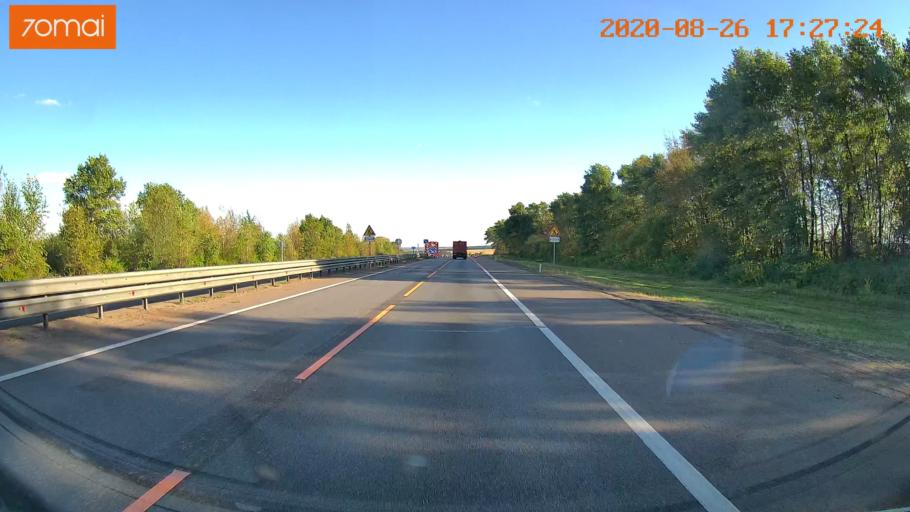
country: RU
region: Tula
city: Kazachka
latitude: 53.4734
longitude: 38.1243
